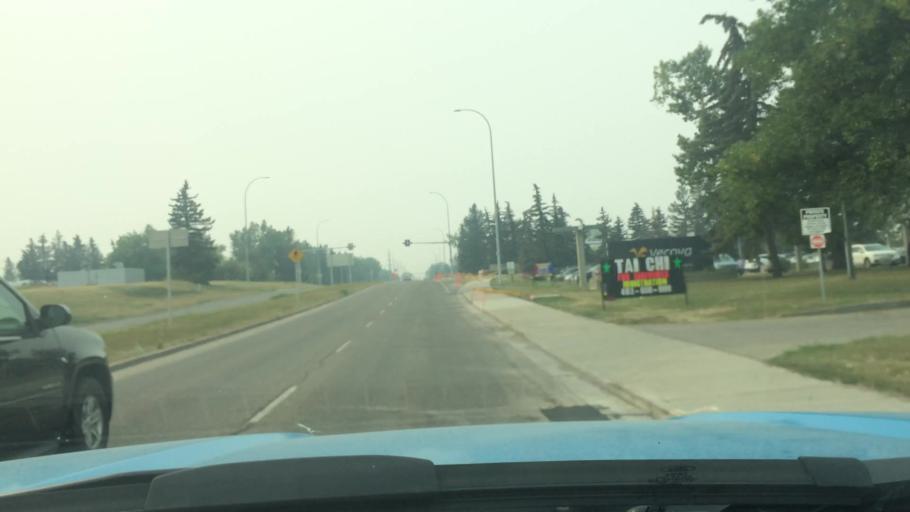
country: CA
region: Alberta
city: Calgary
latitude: 51.0816
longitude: -114.1322
